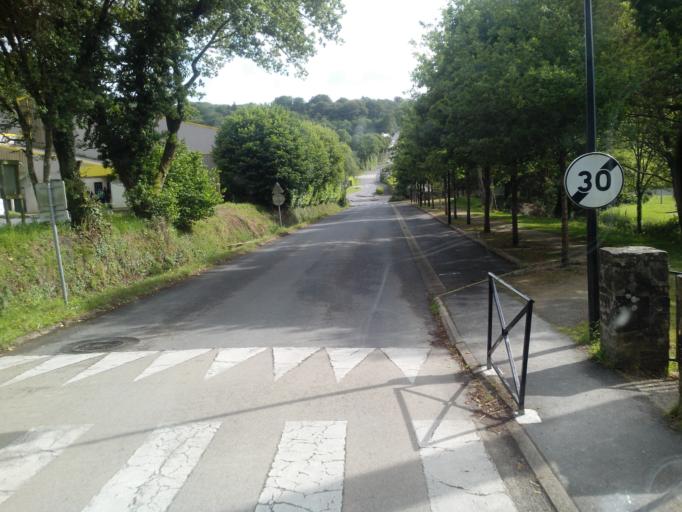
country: FR
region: Brittany
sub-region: Departement du Finistere
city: La Roche-Maurice
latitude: 48.4707
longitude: -4.2039
